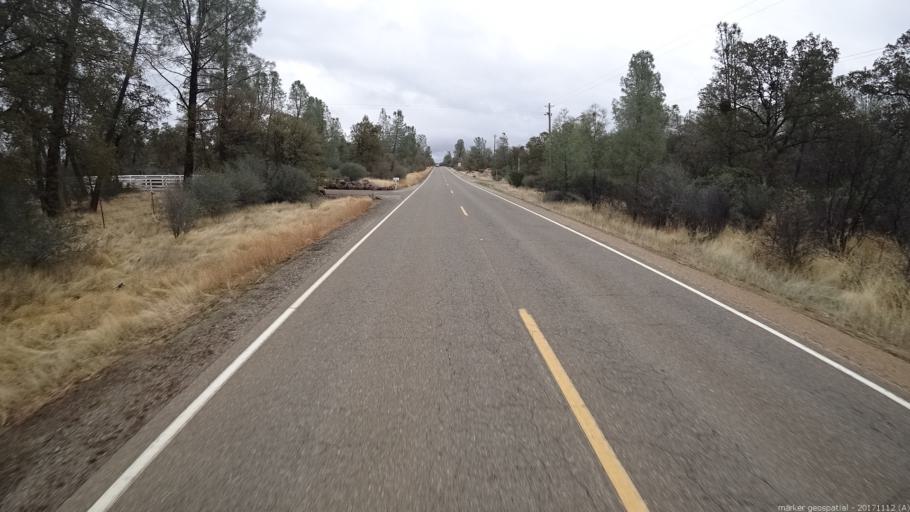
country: US
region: California
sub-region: Shasta County
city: Shingletown
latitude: 40.4933
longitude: -122.0512
